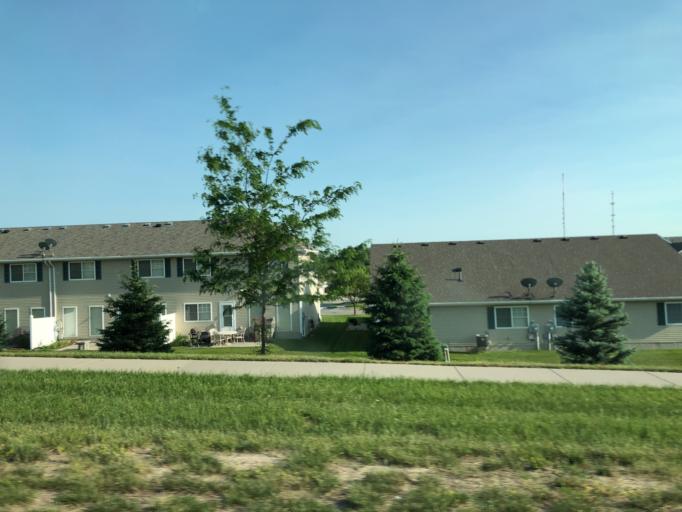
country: US
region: Nebraska
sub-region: Douglas County
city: Elkhorn
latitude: 41.2775
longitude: -96.1910
